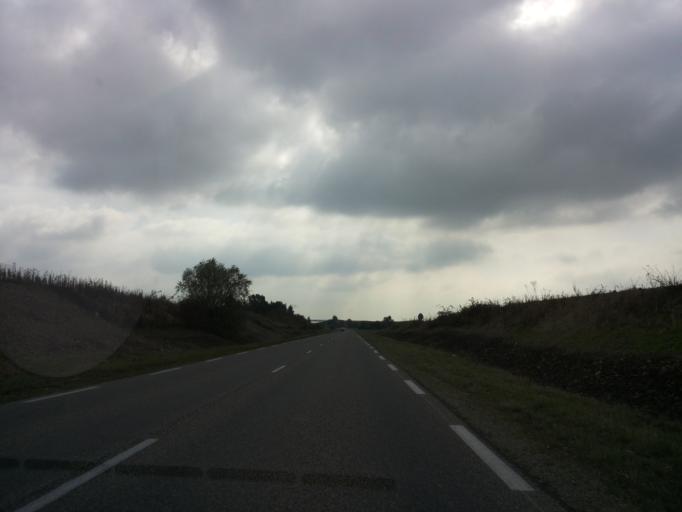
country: FR
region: Lorraine
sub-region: Departement de la Moselle
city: Solgne
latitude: 48.9151
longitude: 6.3368
